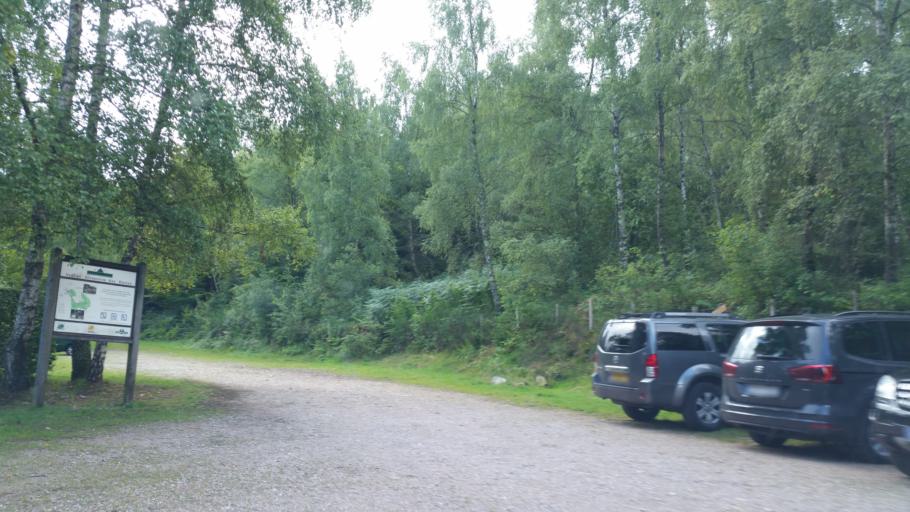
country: FR
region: Lorraine
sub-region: Departement des Vosges
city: Granges-sur-Vologne
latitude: 48.1174
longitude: 6.7836
